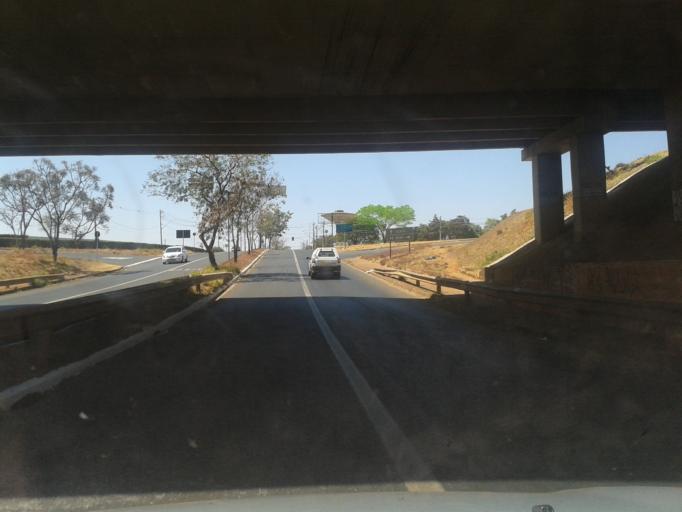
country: BR
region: Minas Gerais
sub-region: Uberlandia
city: Uberlandia
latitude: -18.9253
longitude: -48.2217
